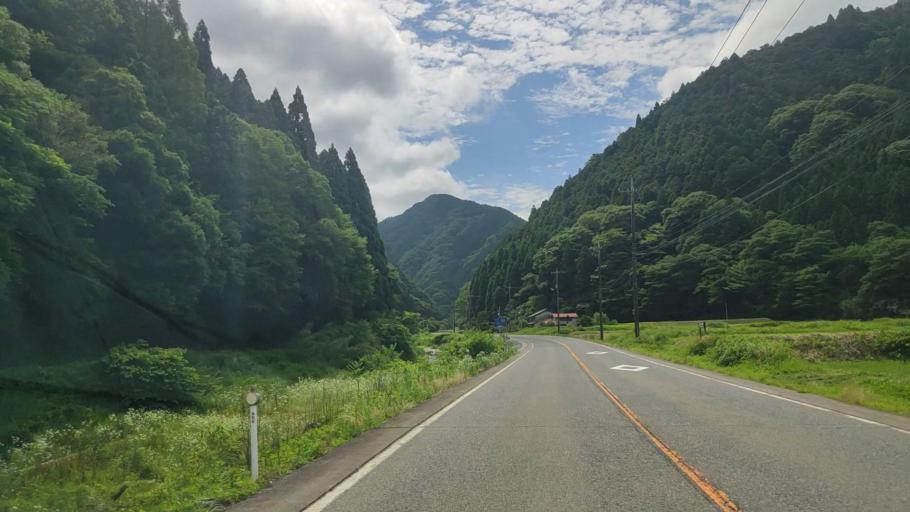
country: JP
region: Okayama
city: Niimi
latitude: 35.2158
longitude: 133.4608
